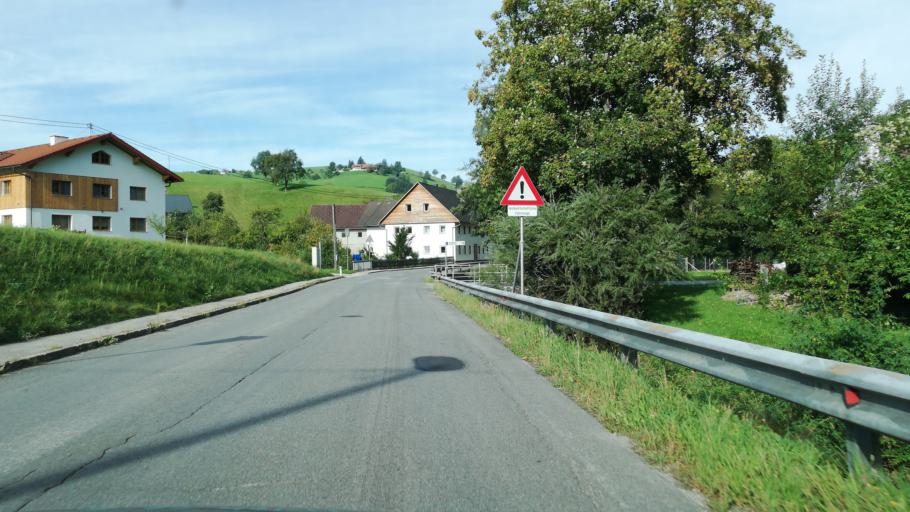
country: AT
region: Upper Austria
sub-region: Politischer Bezirk Steyr-Land
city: Maria Neustift
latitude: 47.9729
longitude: 14.5705
